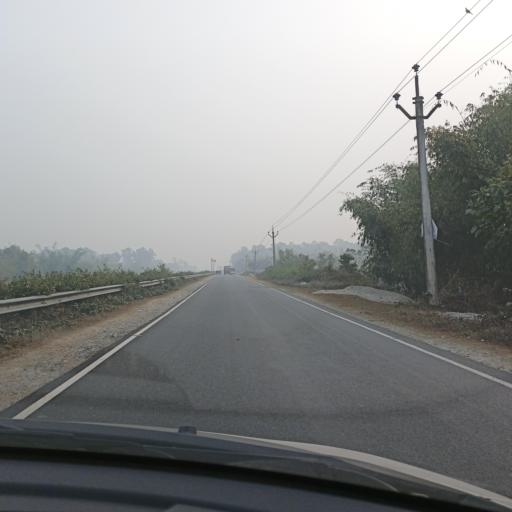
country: IN
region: West Bengal
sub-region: Darjiling
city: Shiliguri
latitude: 26.6767
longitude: 88.5400
